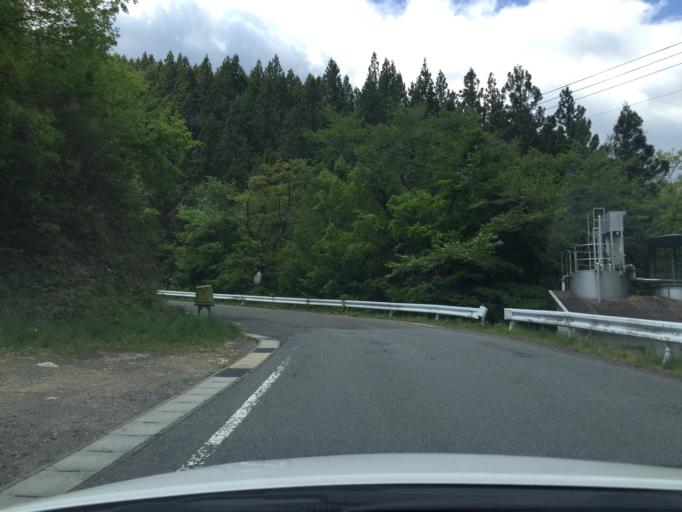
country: JP
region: Fukushima
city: Hobaramachi
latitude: 37.7276
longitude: 140.6413
